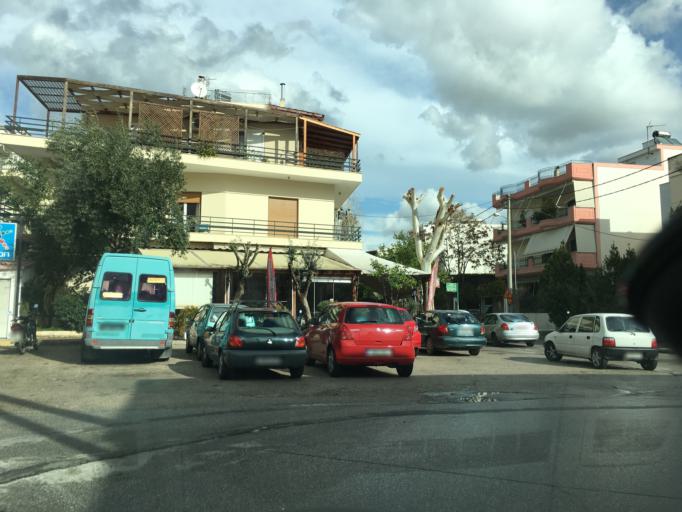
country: GR
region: Attica
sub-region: Nomarchia Athinas
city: Irakleio
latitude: 38.0390
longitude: 23.7727
